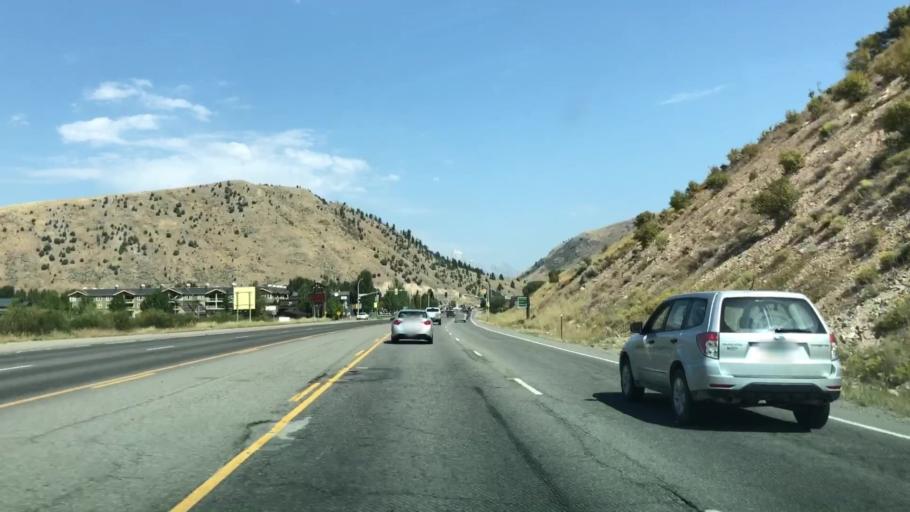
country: US
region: Wyoming
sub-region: Teton County
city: Rafter J Ranch
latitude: 43.4564
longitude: -110.7933
